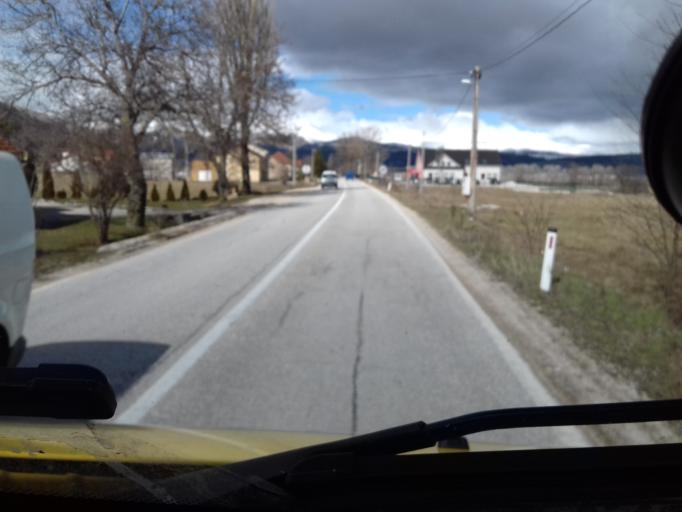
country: BA
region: Federation of Bosnia and Herzegovina
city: Tomislavgrad
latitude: 43.6636
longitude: 17.2077
